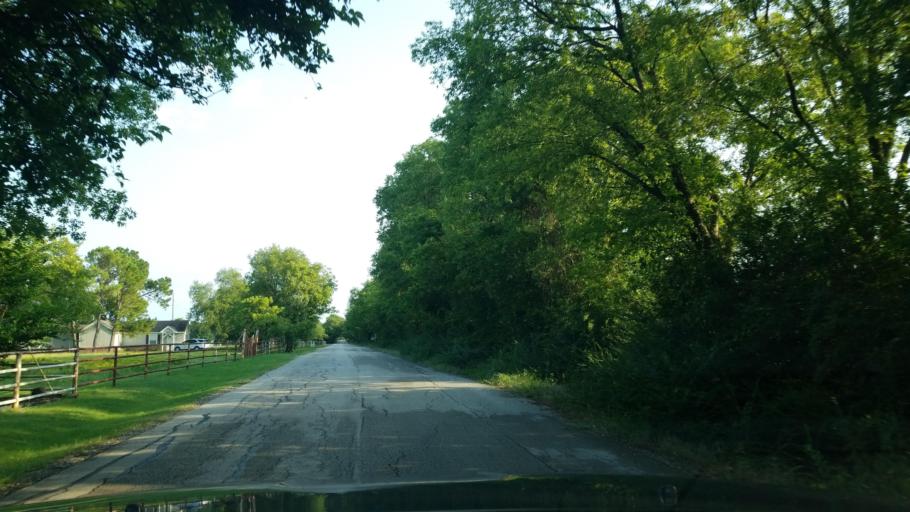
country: US
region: Texas
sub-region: Denton County
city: Cross Roads
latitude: 33.2538
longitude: -97.0613
